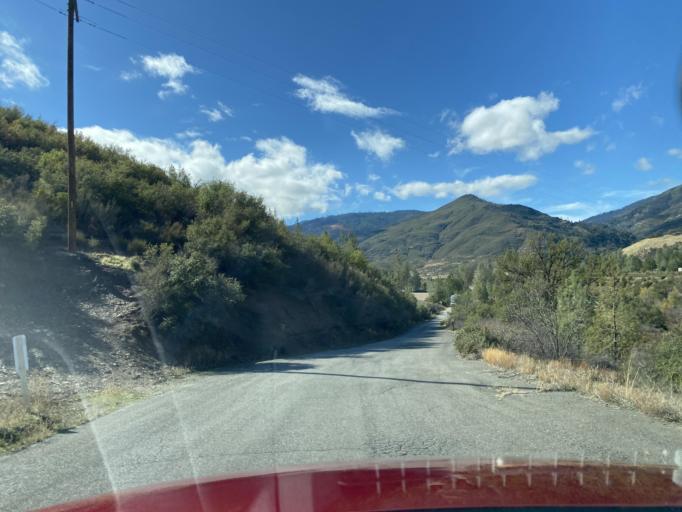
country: US
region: California
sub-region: Lake County
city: Lucerne
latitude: 39.3566
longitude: -122.6522
